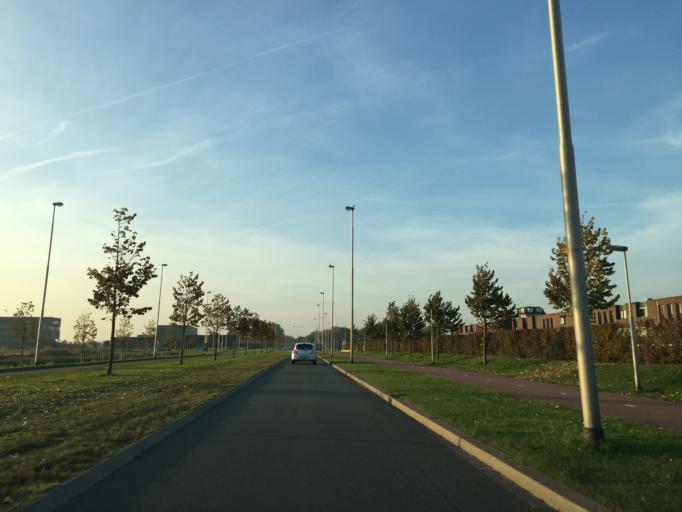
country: NL
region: South Holland
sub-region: Gemeente Lansingerland
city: Berkel en Rodenrijs
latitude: 51.9858
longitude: 4.4868
